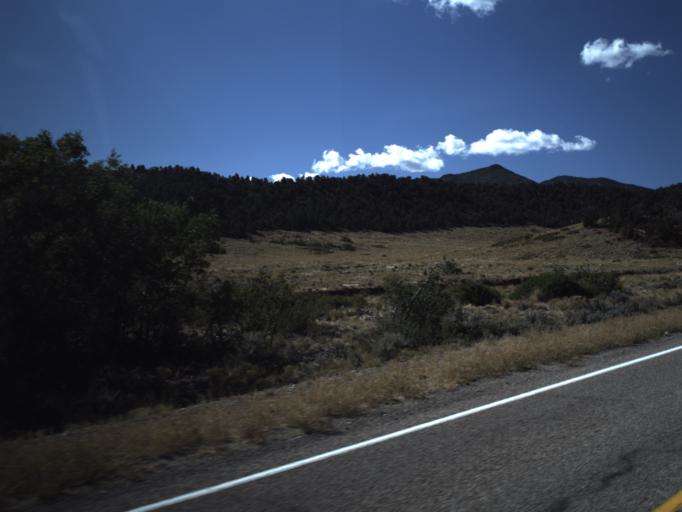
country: US
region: Utah
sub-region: Iron County
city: Cedar City
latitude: 37.6245
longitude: -113.3192
